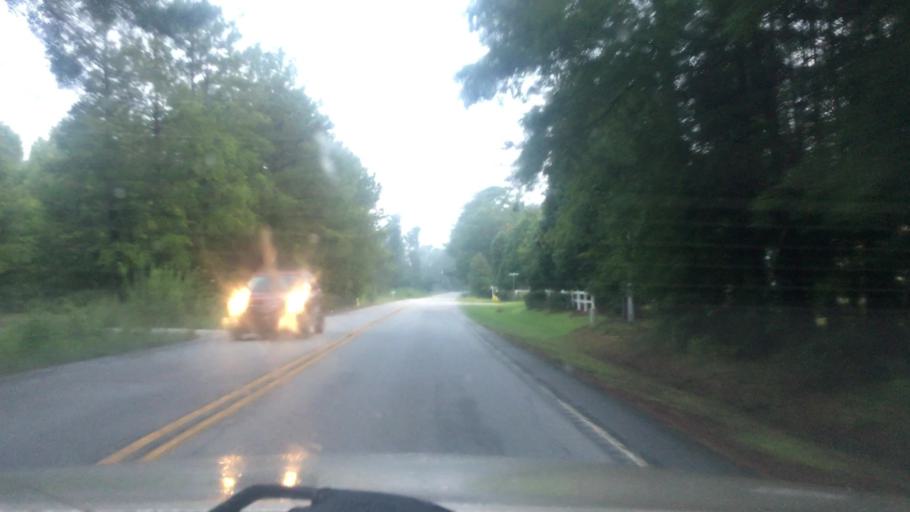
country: US
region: South Carolina
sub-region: Lexington County
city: Irmo
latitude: 34.1189
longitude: -81.1699
